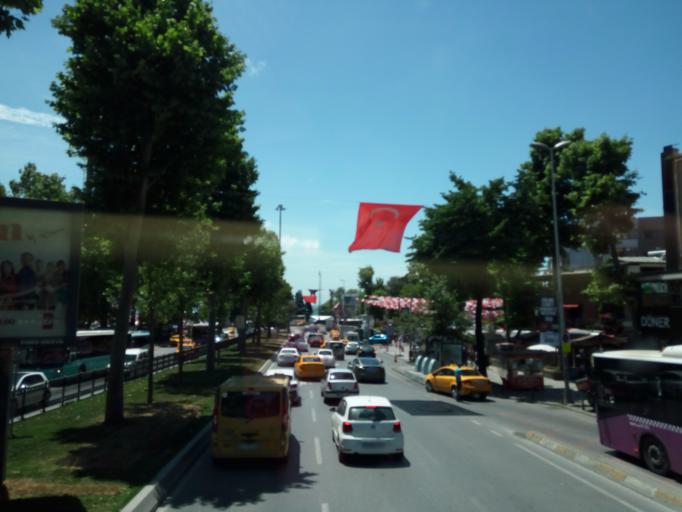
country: TR
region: Istanbul
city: Sisli
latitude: 41.0437
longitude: 29.0071
